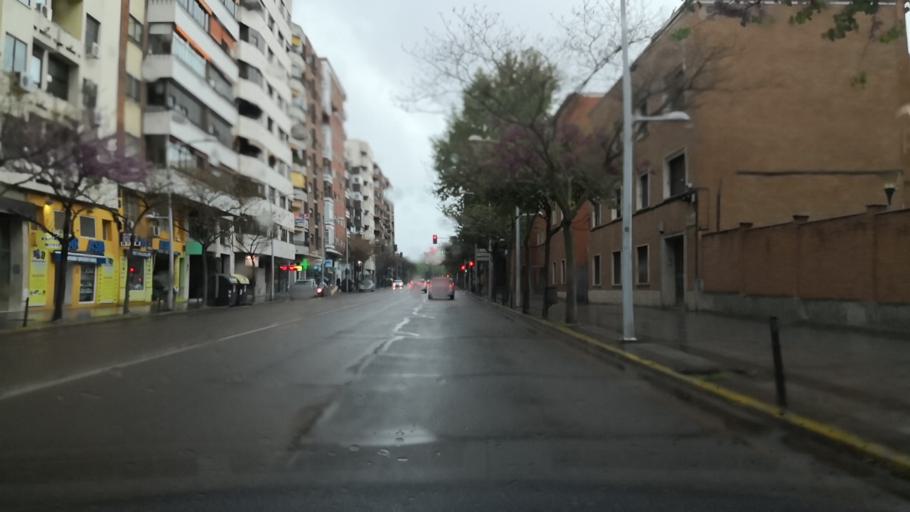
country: ES
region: Extremadura
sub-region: Provincia de Badajoz
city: Badajoz
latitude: 38.8719
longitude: -6.9729
